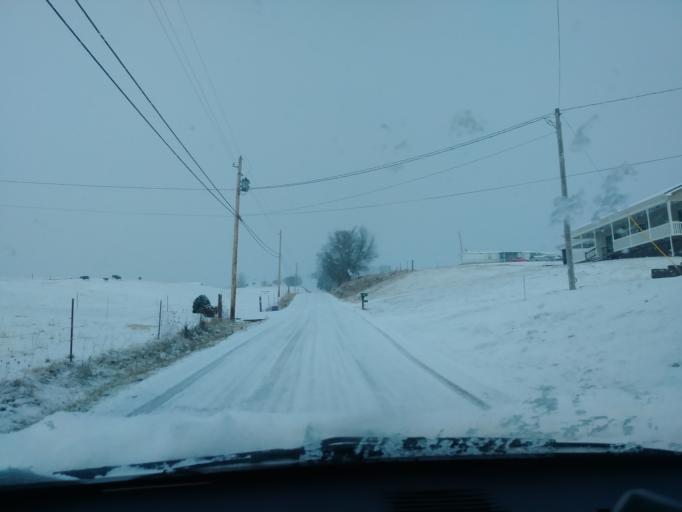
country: US
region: Tennessee
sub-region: Greene County
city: Mosheim
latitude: 36.0927
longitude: -82.9189
